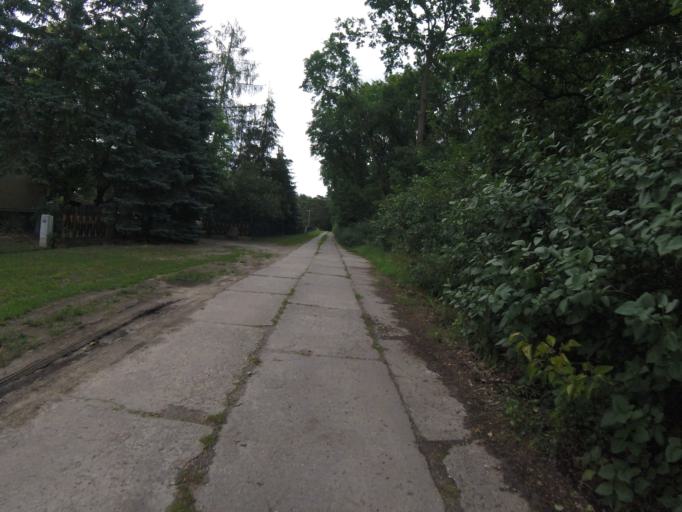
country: DE
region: Brandenburg
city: Konigs Wusterhausen
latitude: 52.3008
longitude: 13.6384
